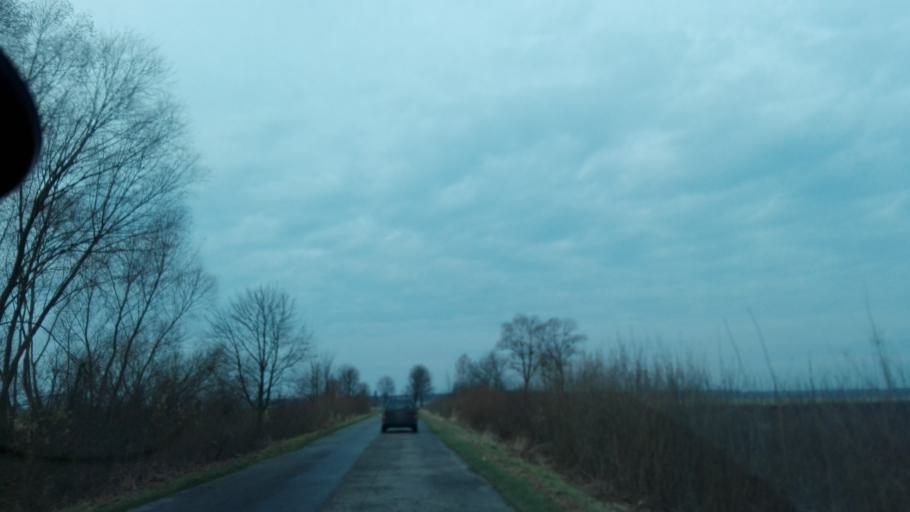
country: PL
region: Lublin Voivodeship
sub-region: Powiat bialski
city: Sosnowka
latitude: 51.7541
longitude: 23.3181
